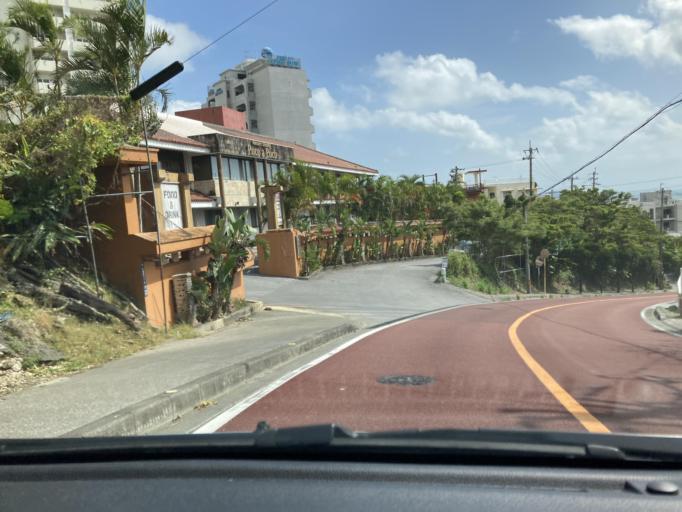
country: JP
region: Okinawa
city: Okinawa
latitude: 26.3210
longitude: 127.8088
